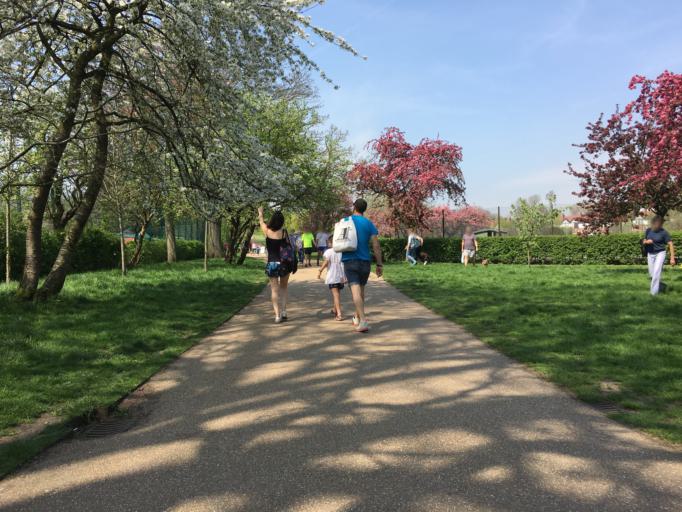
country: GB
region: England
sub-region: Greater London
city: Camden Town
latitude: 51.5593
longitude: -0.1504
